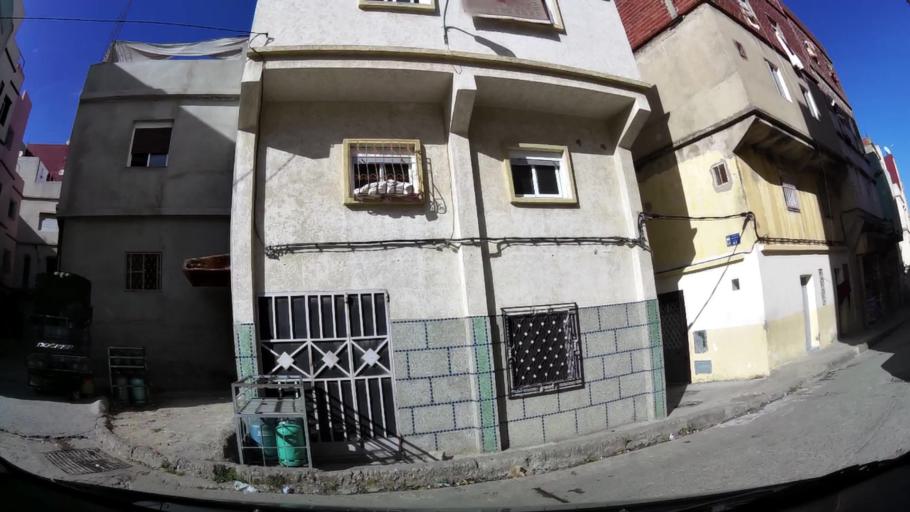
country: MA
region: Tanger-Tetouan
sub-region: Tanger-Assilah
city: Tangier
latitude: 35.7454
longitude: -5.8035
